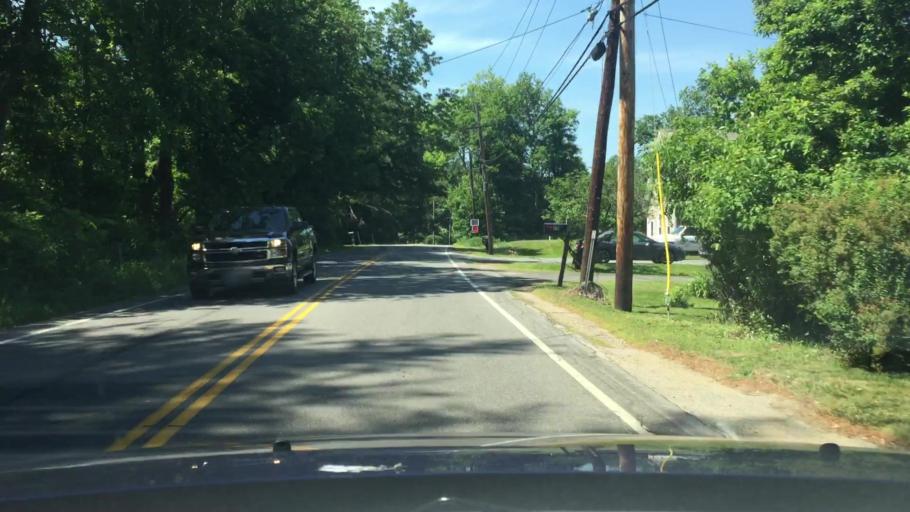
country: US
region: New Hampshire
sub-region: Rockingham County
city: Plaistow
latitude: 42.8130
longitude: -71.0921
